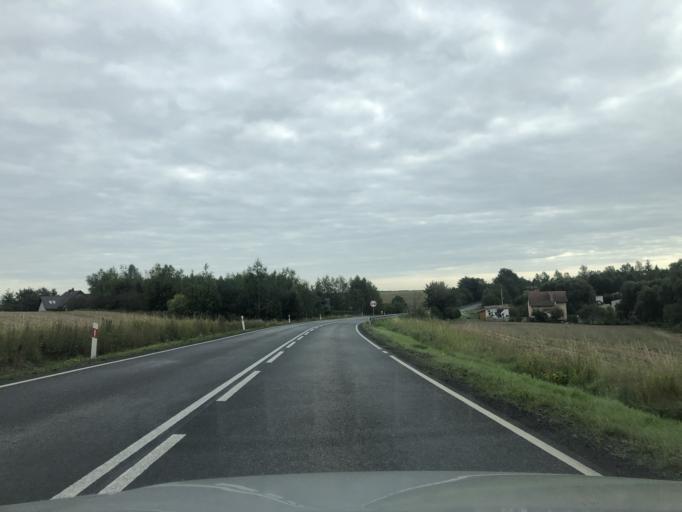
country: PL
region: Greater Poland Voivodeship
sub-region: Powiat pilski
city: Pila
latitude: 53.2330
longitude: 16.6877
